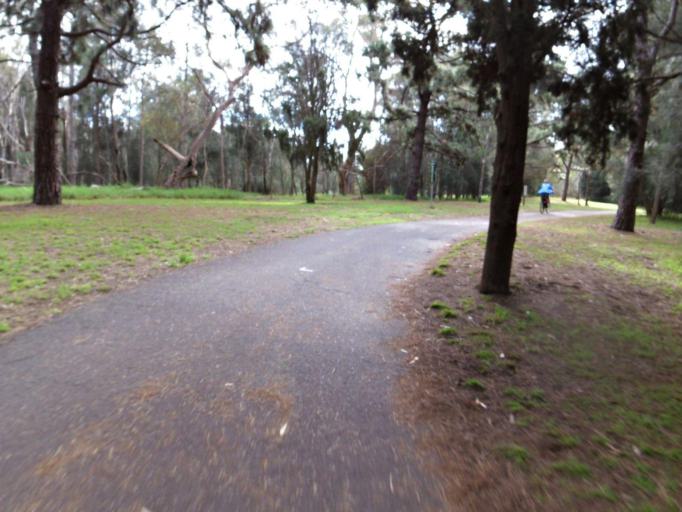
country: AU
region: Victoria
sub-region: Greater Geelong
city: Breakwater
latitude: -38.1698
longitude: 144.3596
